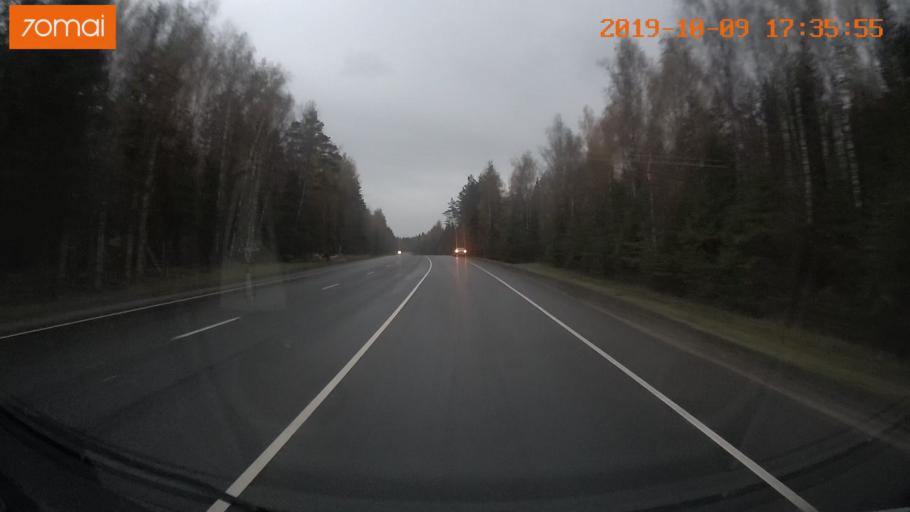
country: RU
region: Ivanovo
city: Bogorodskoye
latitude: 57.0862
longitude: 40.9989
